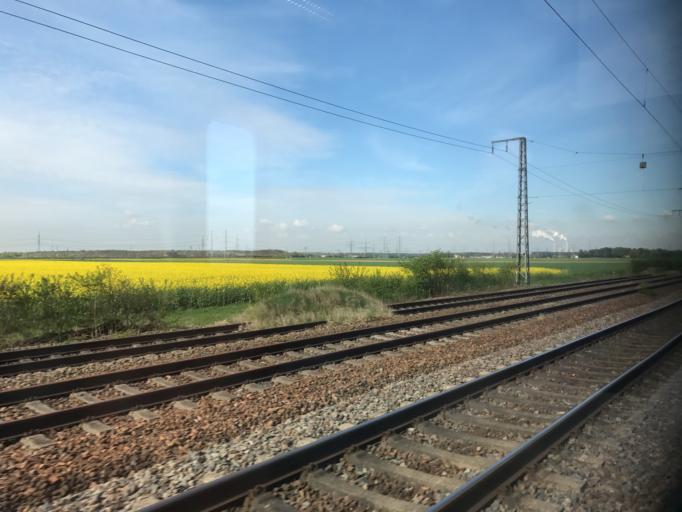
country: DE
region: Baden-Wuerttemberg
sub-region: Karlsruhe Region
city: Edingen-Neckarhausen
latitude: 49.4286
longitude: 8.5974
